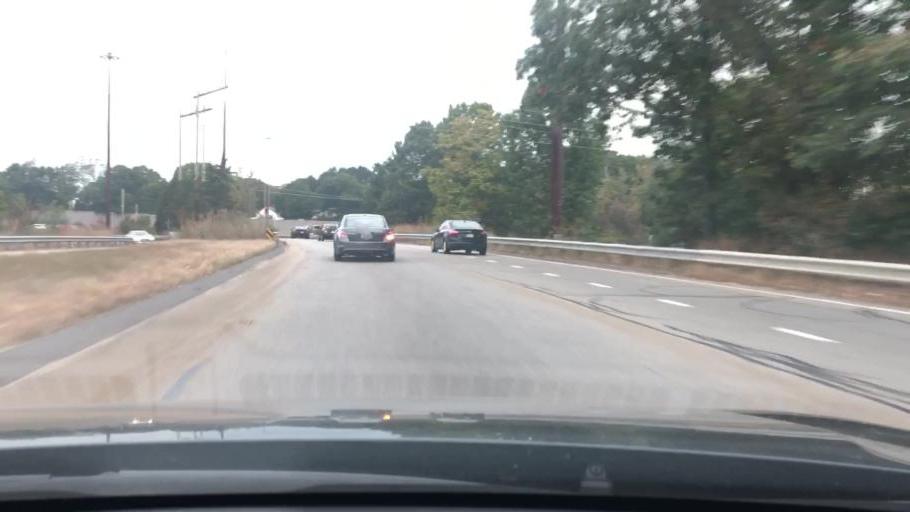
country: US
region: Massachusetts
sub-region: Middlesex County
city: Lowell
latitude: 42.6087
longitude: -71.3240
